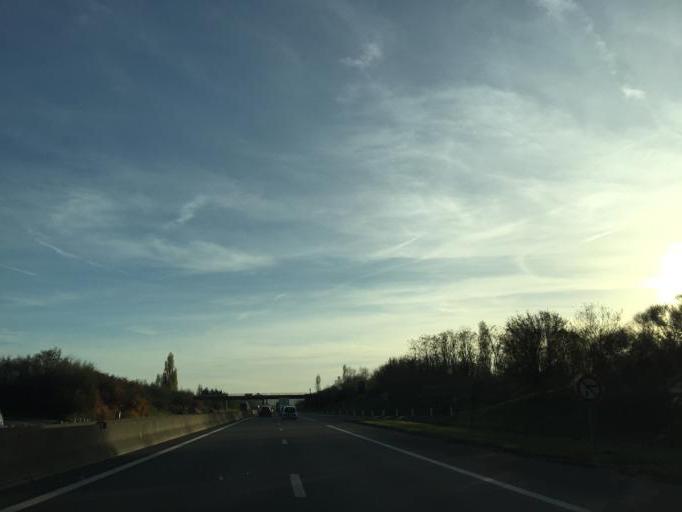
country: FR
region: Rhone-Alpes
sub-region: Departement du Rhone
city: Mions
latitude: 45.6621
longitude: 4.9231
